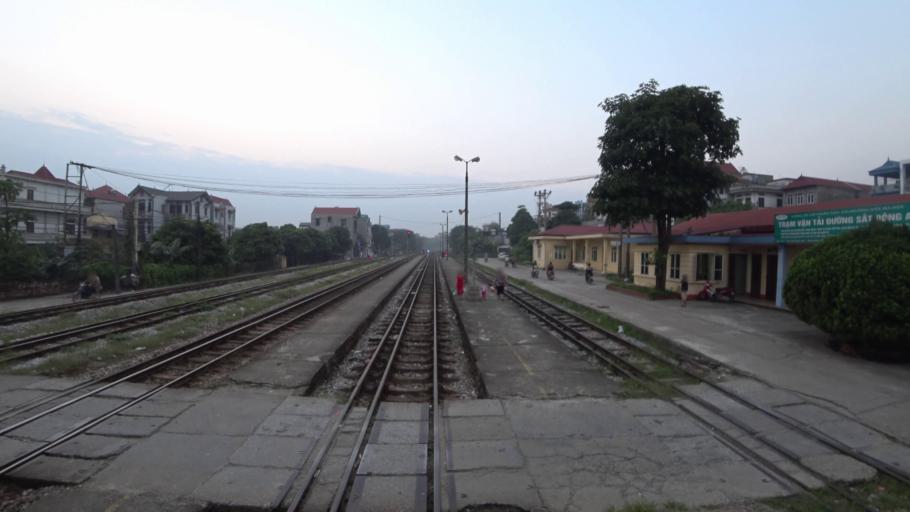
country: VN
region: Ha Noi
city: Dong Anh
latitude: 21.1919
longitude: 105.8552
